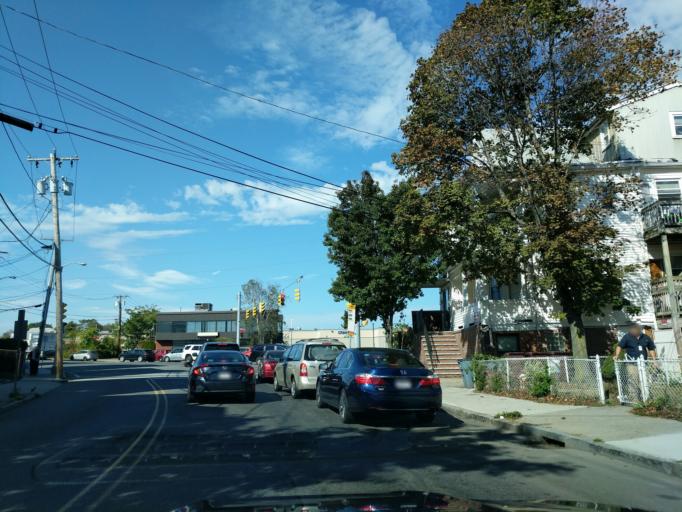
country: US
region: Massachusetts
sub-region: Suffolk County
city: Revere
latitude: 42.4099
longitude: -70.9987
